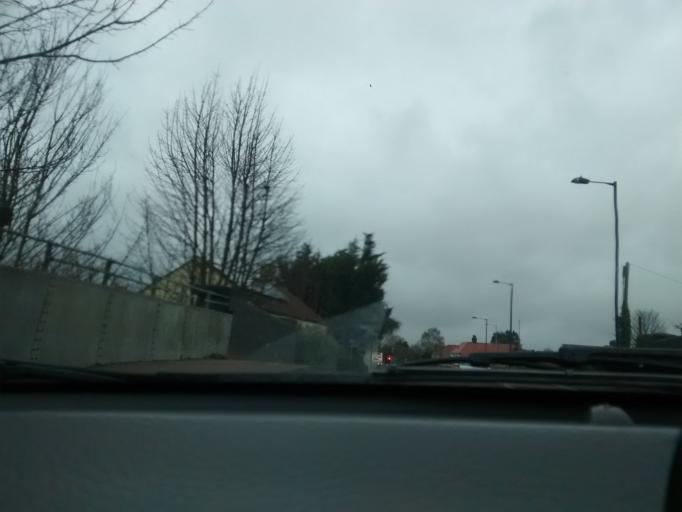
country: GB
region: England
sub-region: Suffolk
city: Felixstowe
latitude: 51.9668
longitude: 1.3463
